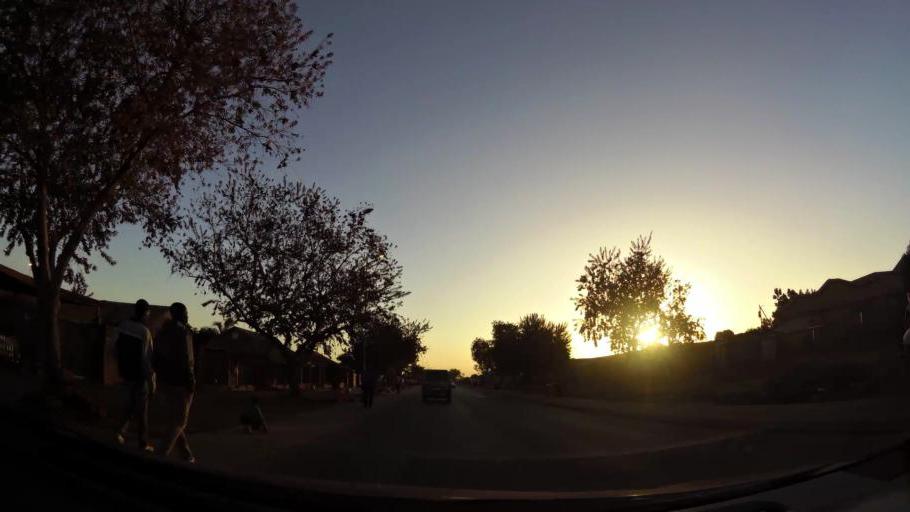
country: ZA
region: Gauteng
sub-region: City of Tshwane Metropolitan Municipality
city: Mabopane
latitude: -25.5817
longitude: 28.0831
